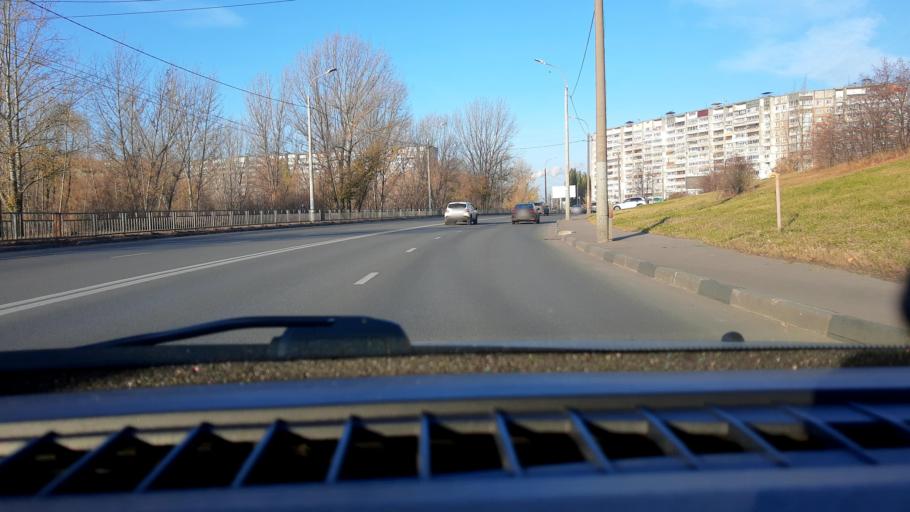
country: RU
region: Nizjnij Novgorod
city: Nizhniy Novgorod
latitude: 56.3415
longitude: 43.9349
